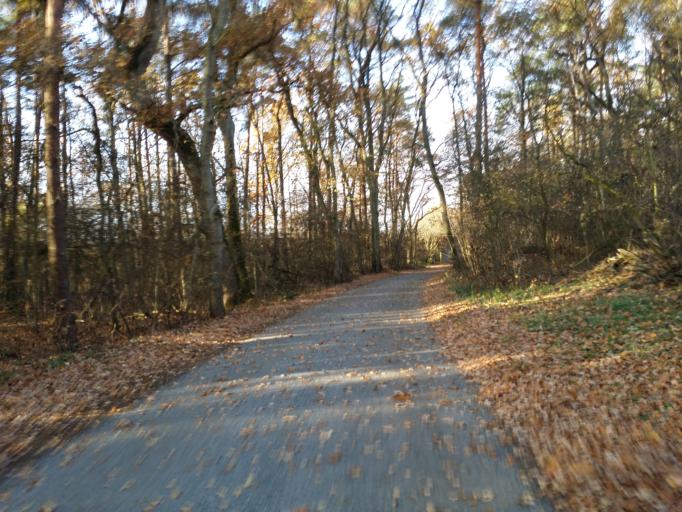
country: DE
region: Lower Saxony
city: Ahausen
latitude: 53.0971
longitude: 9.3459
